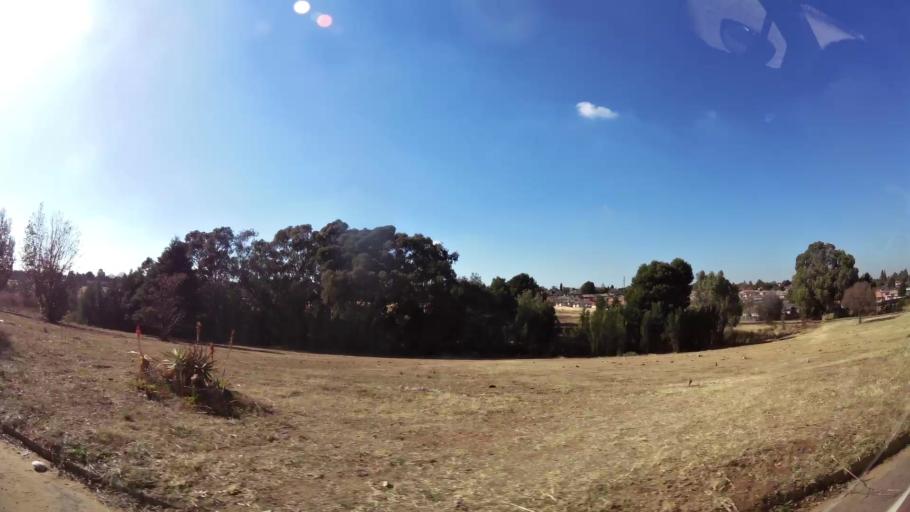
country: ZA
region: Gauteng
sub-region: City of Johannesburg Metropolitan Municipality
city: Roodepoort
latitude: -26.1384
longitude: 27.8212
